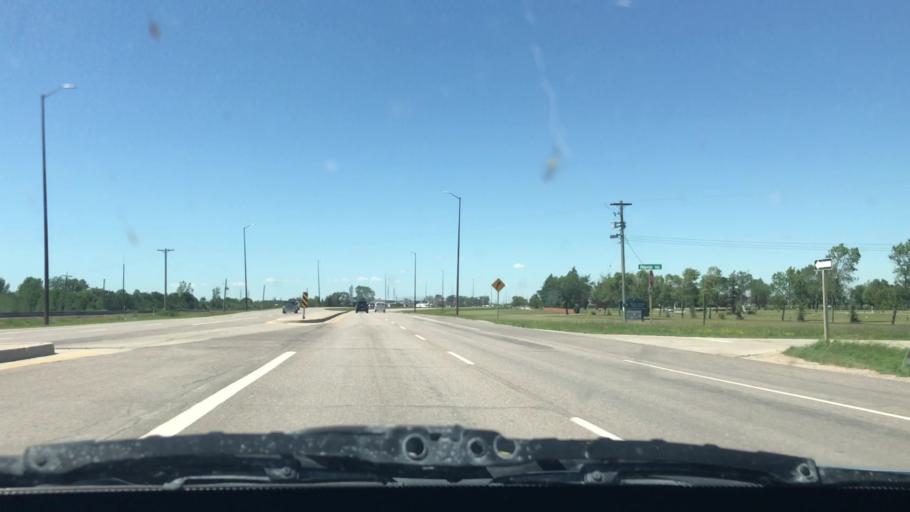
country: CA
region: Manitoba
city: Winnipeg
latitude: 49.8411
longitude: -96.9864
